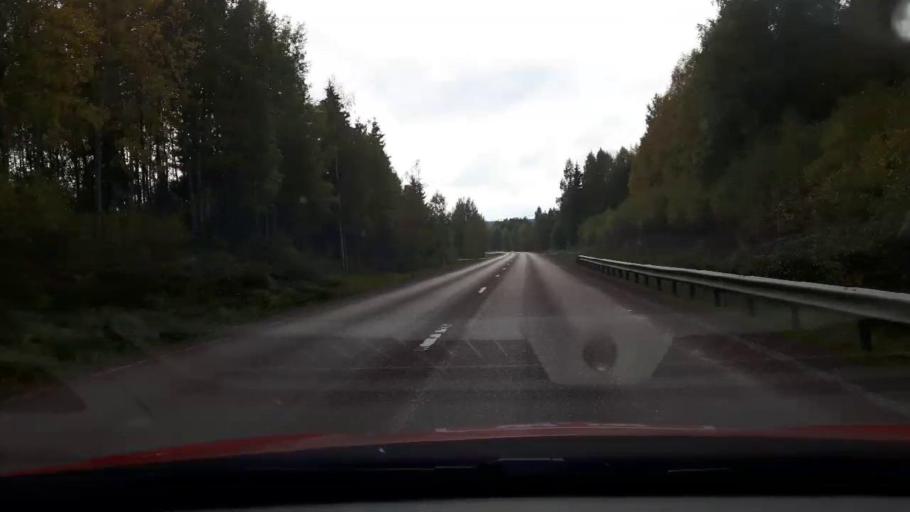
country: SE
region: Gaevleborg
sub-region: Ljusdals Kommun
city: Jaervsoe
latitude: 61.6123
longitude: 16.2954
